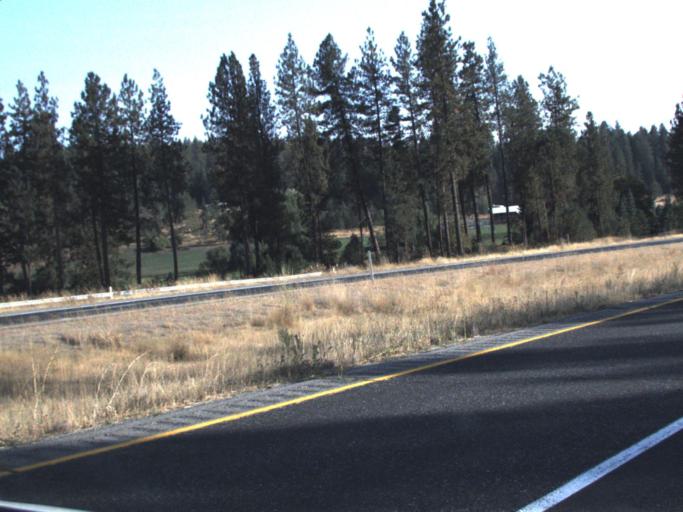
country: US
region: Washington
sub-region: Spokane County
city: Mead
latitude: 47.8946
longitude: -117.3530
